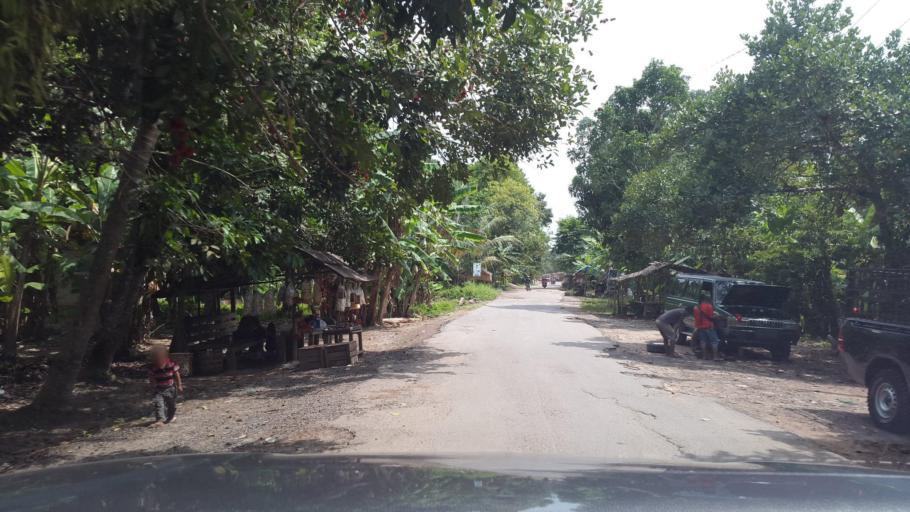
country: ID
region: South Sumatra
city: Tanjung Lubuk
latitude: -3.2640
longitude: 104.8682
